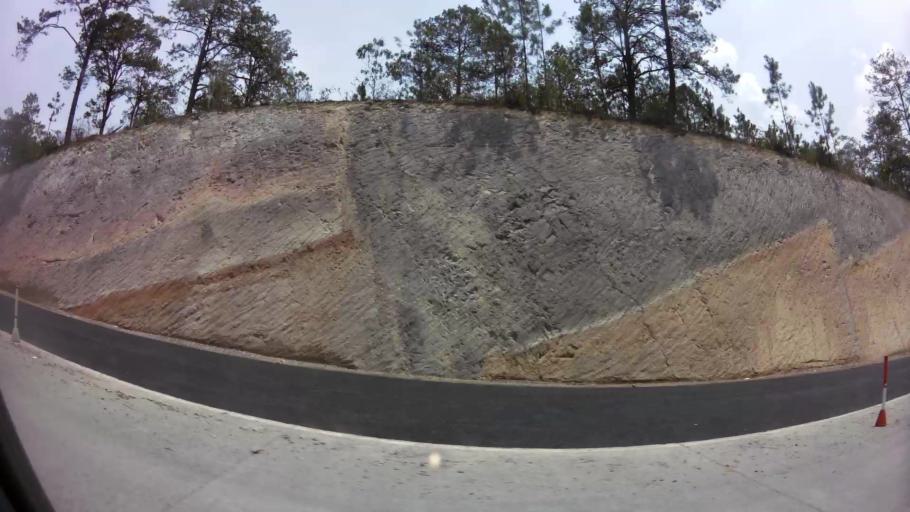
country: HN
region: Comayagua
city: El Socorro
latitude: 14.6303
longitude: -87.9192
